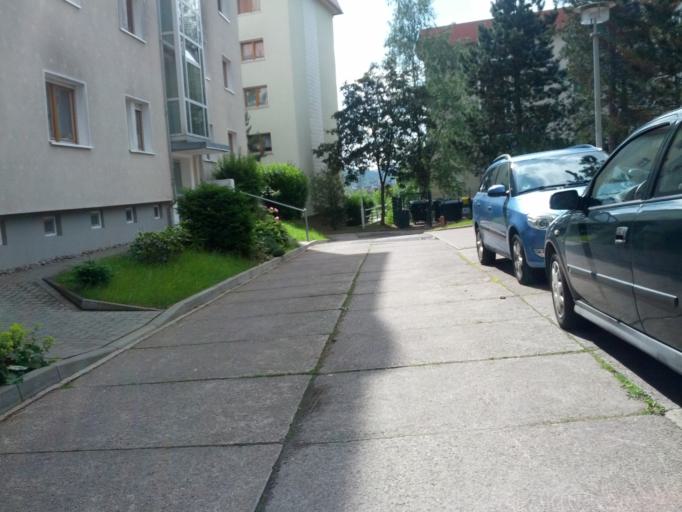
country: DE
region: Thuringia
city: Eisenach
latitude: 50.9779
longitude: 10.3464
